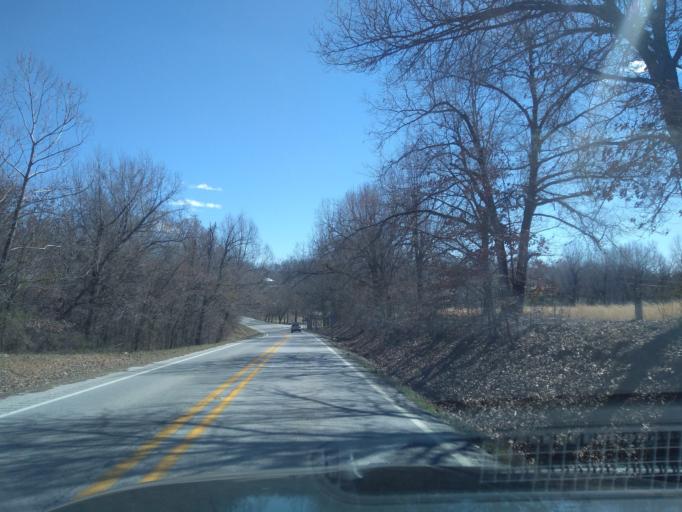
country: US
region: Arkansas
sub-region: Washington County
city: Farmington
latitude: 36.0782
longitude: -94.2957
